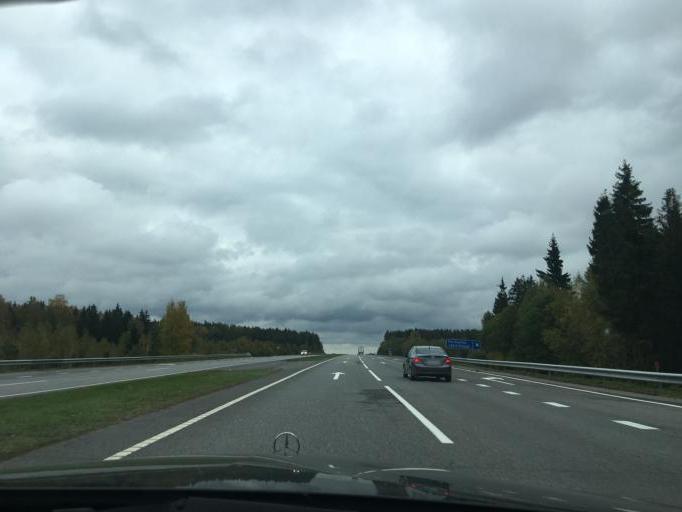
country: BY
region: Vitebsk
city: Kokhanava
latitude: 54.4783
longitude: 29.8456
